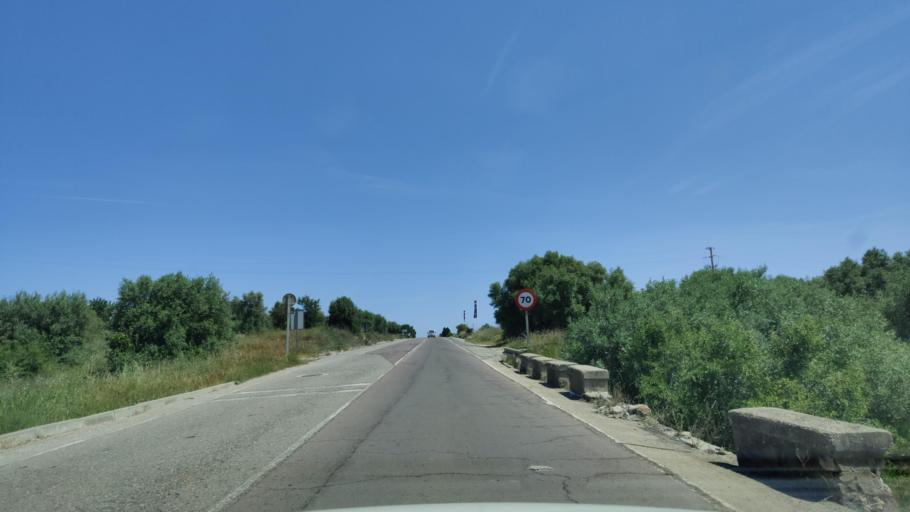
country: ES
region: Catalonia
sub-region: Provincia de Tarragona
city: Sant Carles de la Rapita
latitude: 40.6279
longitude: 0.5966
